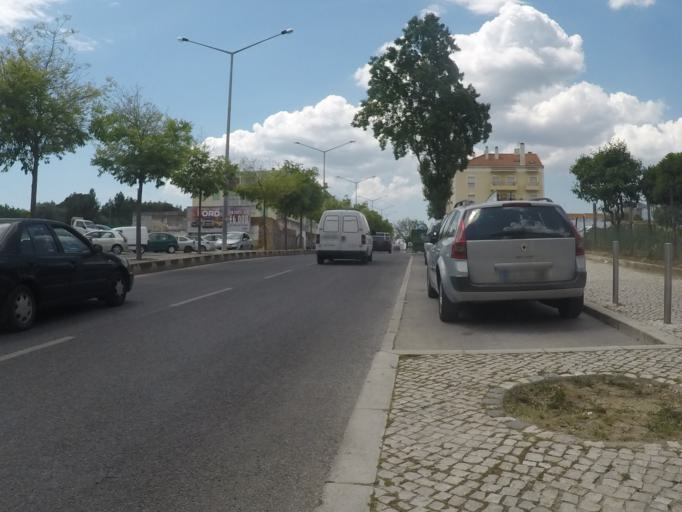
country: PT
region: Setubal
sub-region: Setubal
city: Setubal
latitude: 38.5256
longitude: -8.8723
